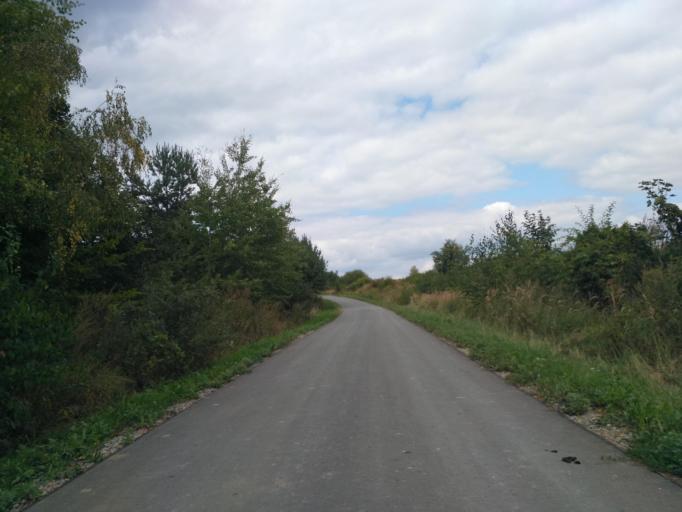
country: PL
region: Subcarpathian Voivodeship
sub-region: Powiat rzeszowski
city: Dynow
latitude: 49.7683
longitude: 22.2869
